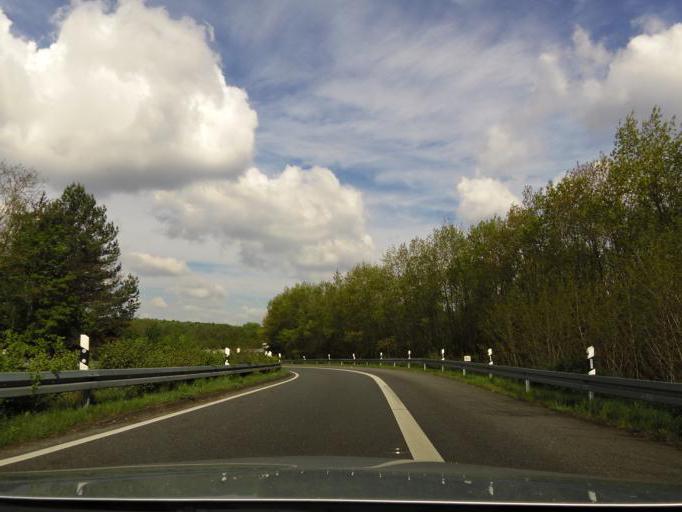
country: DE
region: Hesse
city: Morfelden-Walldorf
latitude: 49.9843
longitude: 8.6034
